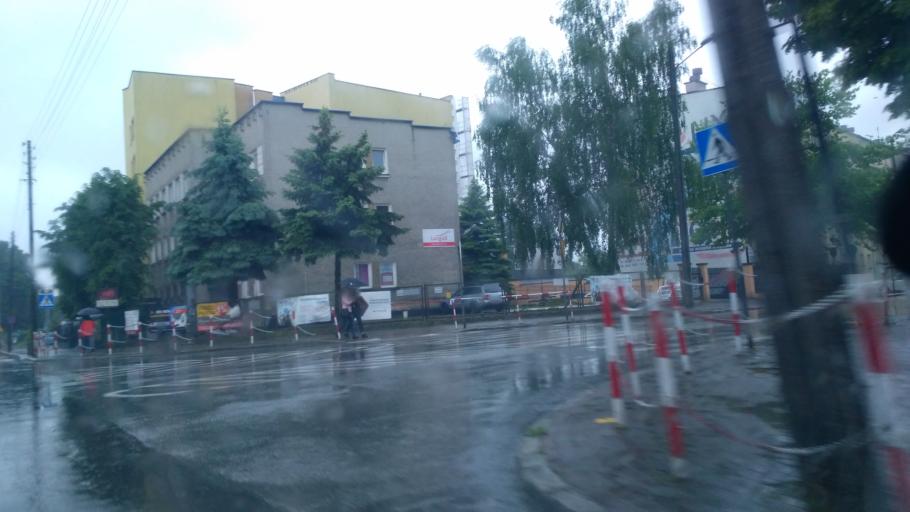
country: PL
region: Subcarpathian Voivodeship
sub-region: Powiat jasielski
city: Jaslo
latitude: 49.7403
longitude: 21.4677
